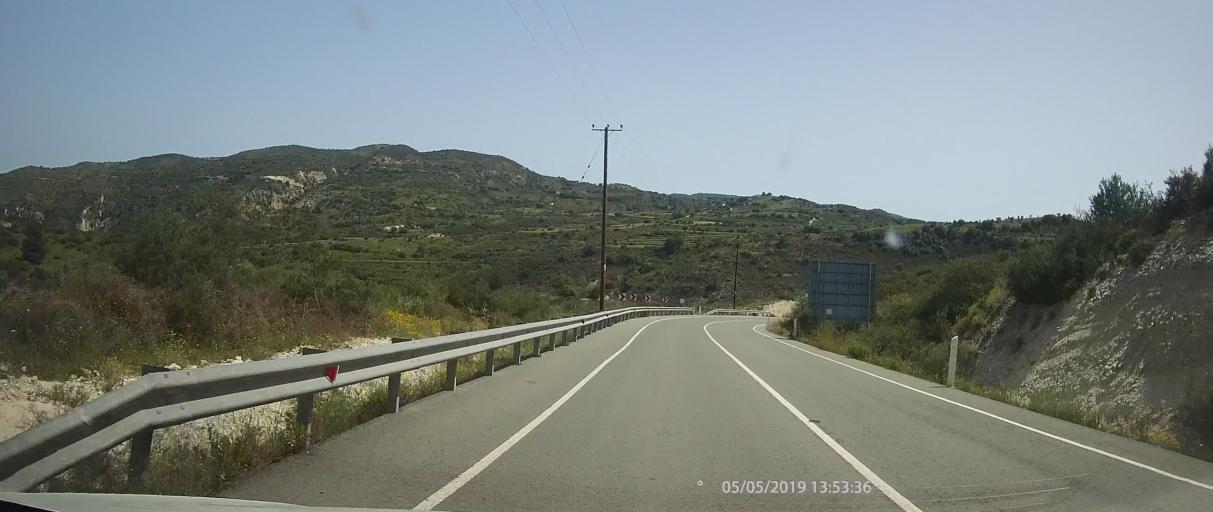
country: CY
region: Limassol
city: Pachna
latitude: 34.8183
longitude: 32.7252
